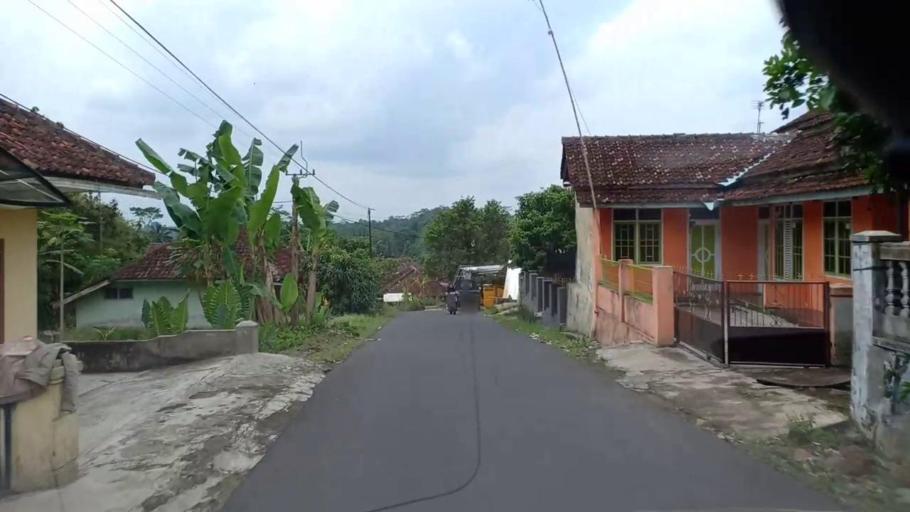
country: ID
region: West Java
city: Gerempay
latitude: -7.3377
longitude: 108.2843
